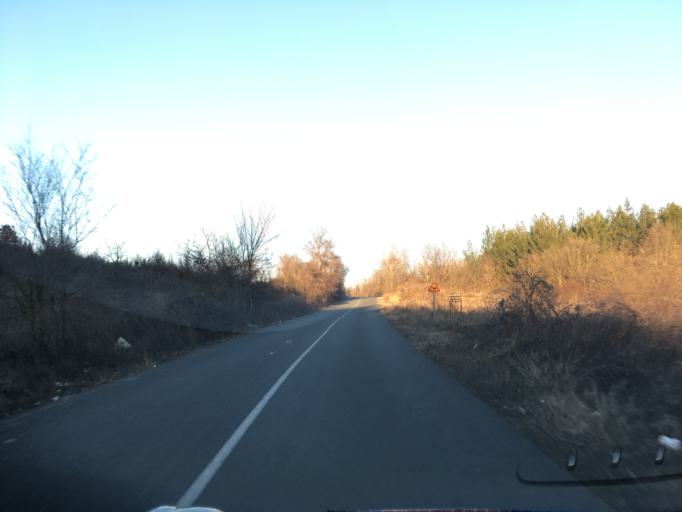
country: GR
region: West Macedonia
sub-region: Nomos Kozanis
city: Koila
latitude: 40.3245
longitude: 21.7977
